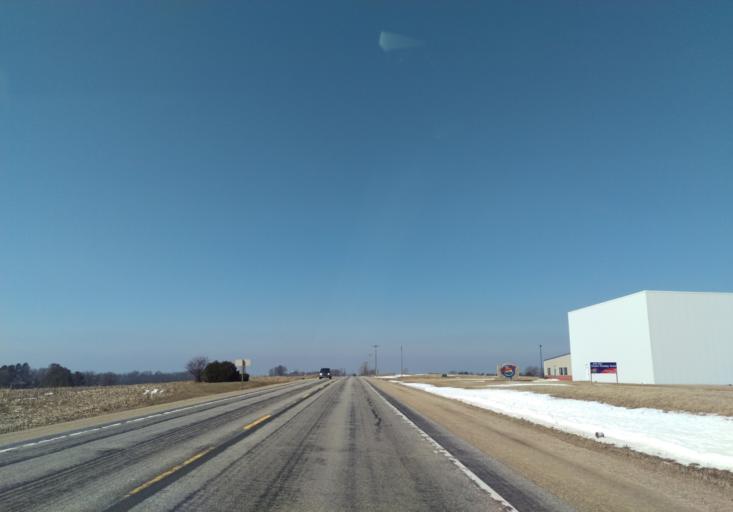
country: US
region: Wisconsin
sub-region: Vernon County
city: Westby
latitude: 43.6625
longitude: -90.8629
